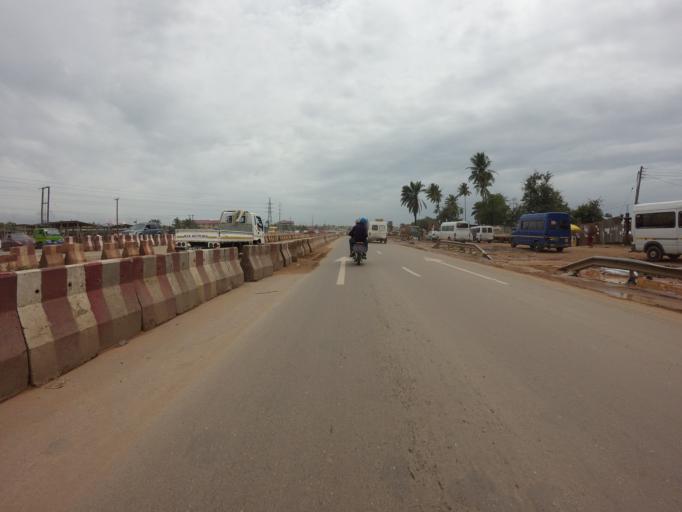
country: GH
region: Greater Accra
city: Achiaman
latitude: 5.6880
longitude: -0.2824
